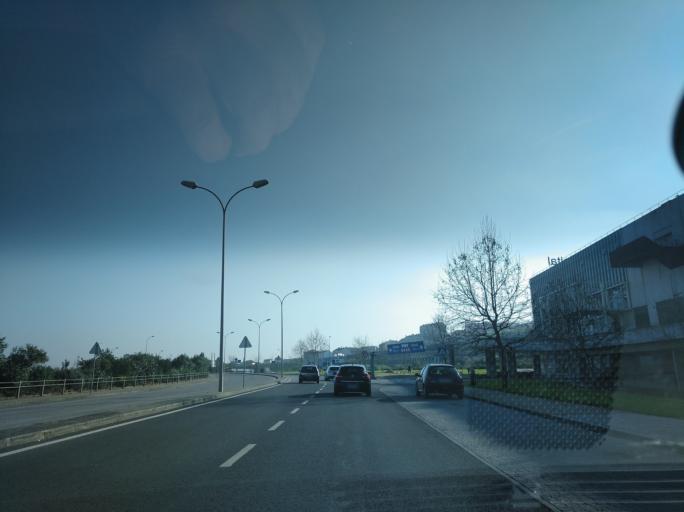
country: PT
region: Lisbon
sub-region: Odivelas
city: Famoes
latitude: 38.7764
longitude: -9.2179
